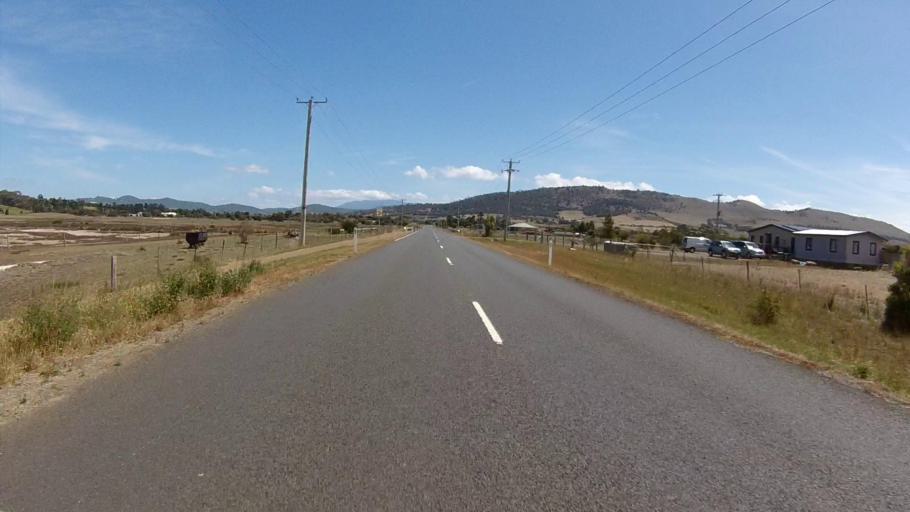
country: AU
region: Tasmania
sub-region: Sorell
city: Sorell
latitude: -42.7766
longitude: 147.5302
